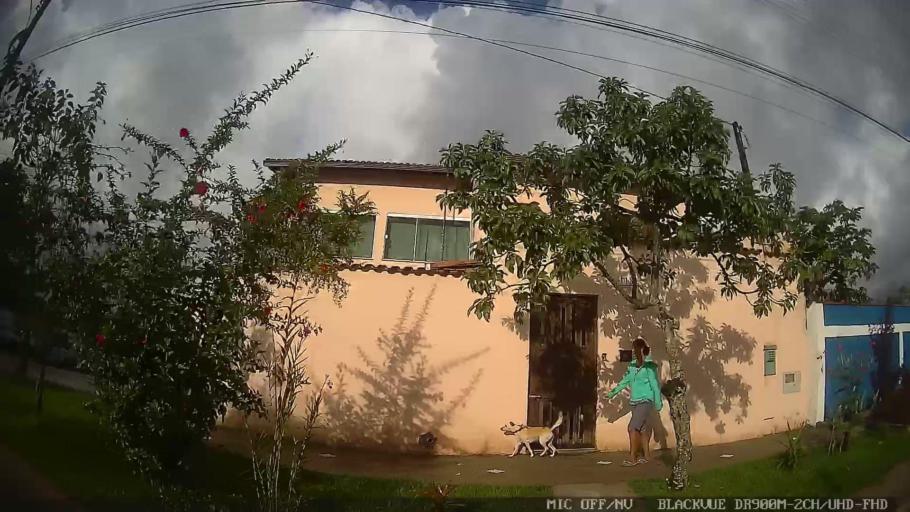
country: BR
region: Sao Paulo
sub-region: Itanhaem
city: Itanhaem
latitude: -24.1989
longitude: -46.8692
